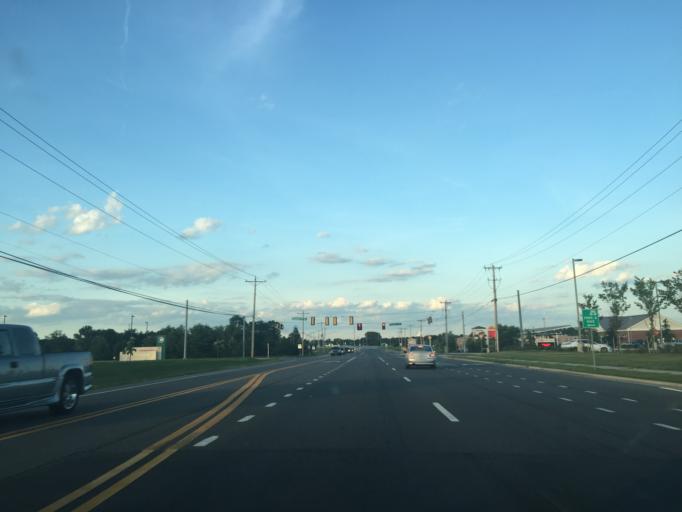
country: US
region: Delaware
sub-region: New Castle County
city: Middletown
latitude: 39.4532
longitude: -75.6828
